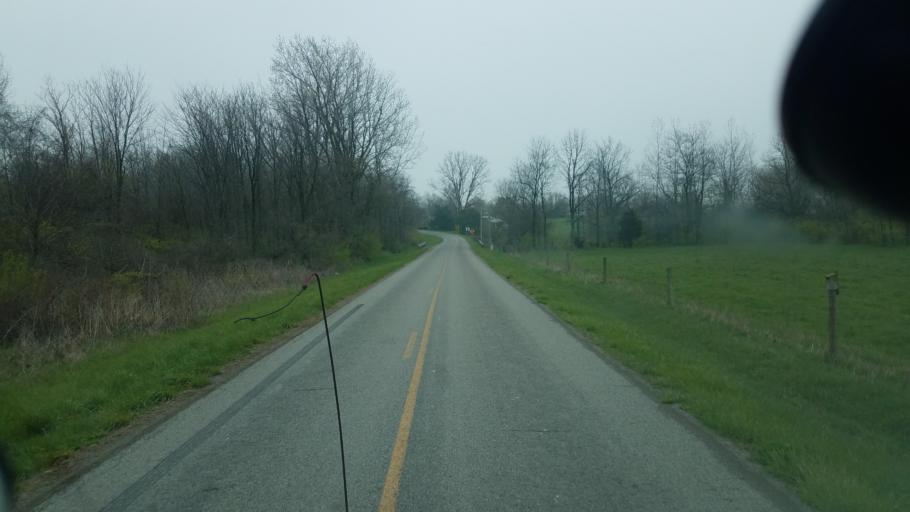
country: US
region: Ohio
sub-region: Logan County
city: Northwood
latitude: 40.4697
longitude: -83.7368
